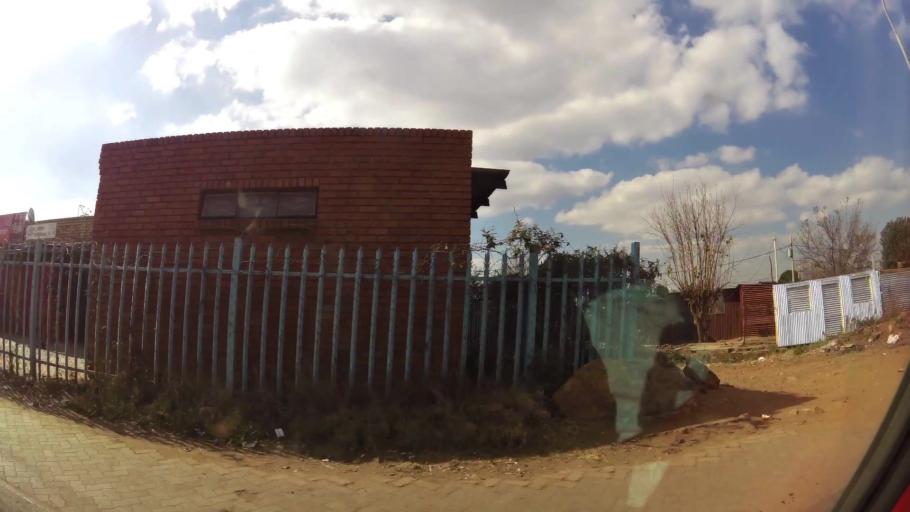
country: ZA
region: Gauteng
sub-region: Ekurhuleni Metropolitan Municipality
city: Tembisa
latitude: -25.9894
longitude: 28.2285
